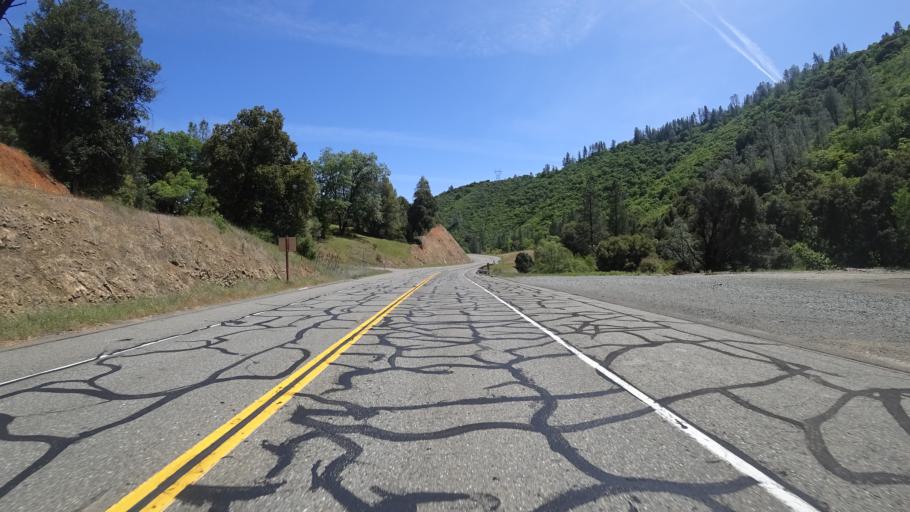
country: US
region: California
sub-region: Trinity County
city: Lewiston
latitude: 40.6727
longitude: -122.6618
